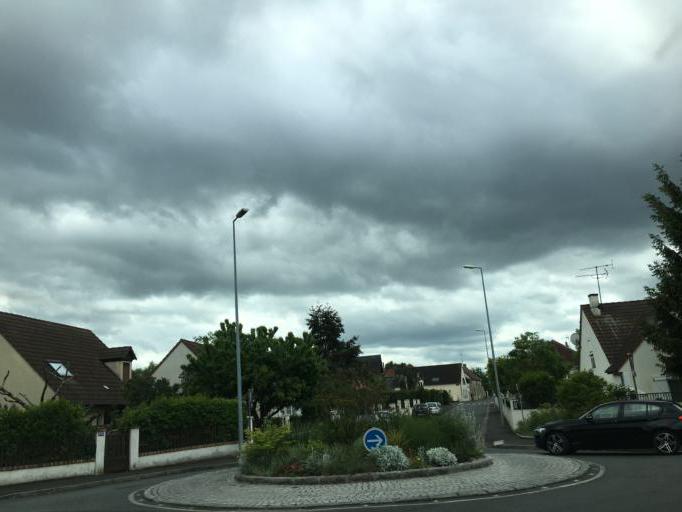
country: FR
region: Centre
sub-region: Departement du Loiret
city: Semoy
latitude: 47.9279
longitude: 1.9379
